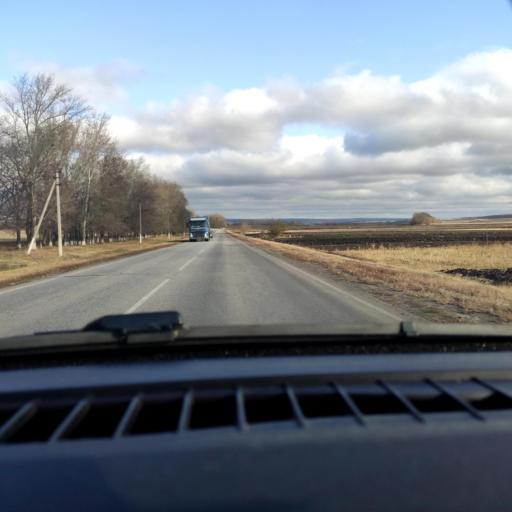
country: RU
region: Belgorod
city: Ilovka
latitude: 50.7350
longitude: 38.7021
